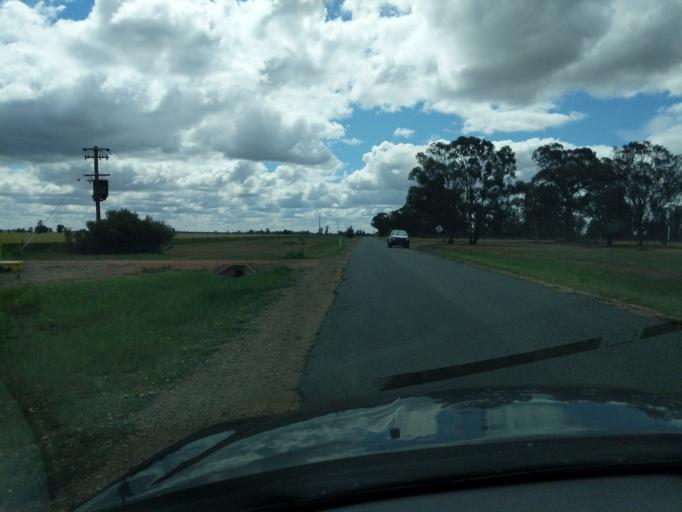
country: AU
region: New South Wales
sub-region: Coolamon
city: Coolamon
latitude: -34.8670
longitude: 146.8967
